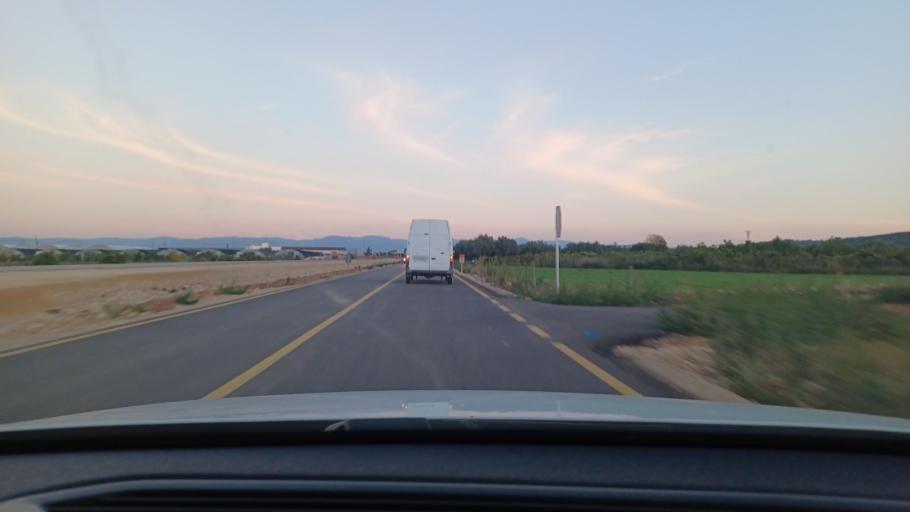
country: ES
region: Catalonia
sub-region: Provincia de Tarragona
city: Alcanar
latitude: 40.5388
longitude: 0.4403
